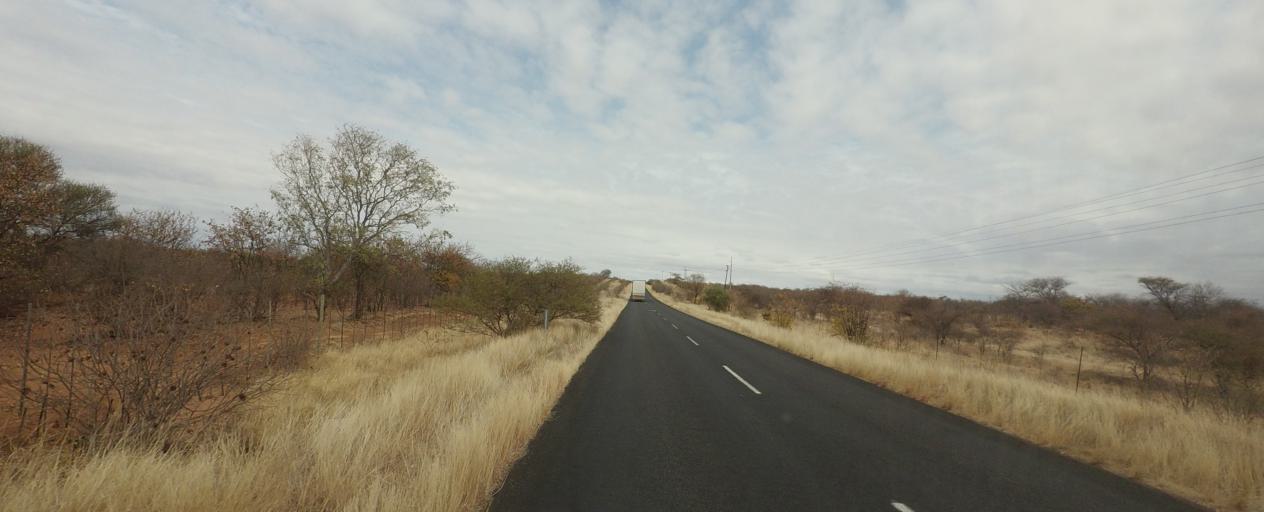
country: ZW
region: Matabeleland South
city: Beitbridge
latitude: -22.4298
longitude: 29.4305
